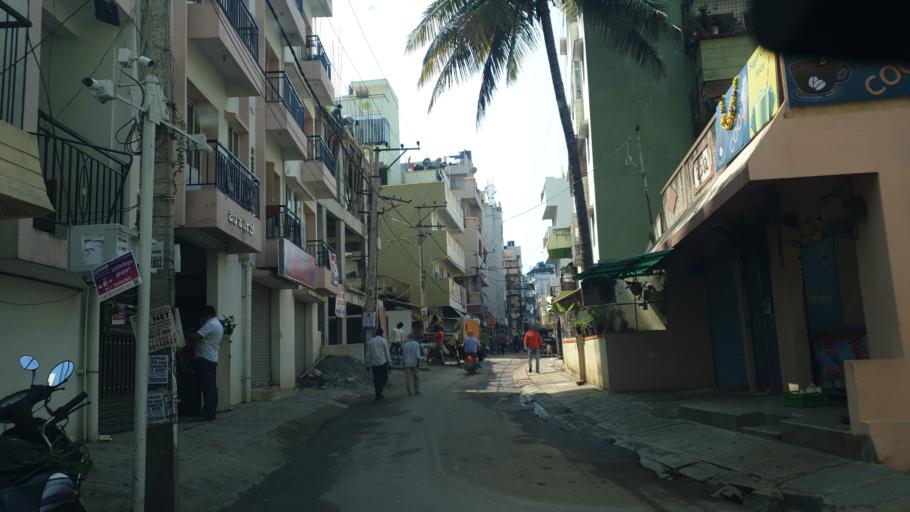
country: IN
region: Karnataka
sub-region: Bangalore Urban
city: Bangalore
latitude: 12.9739
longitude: 77.6657
